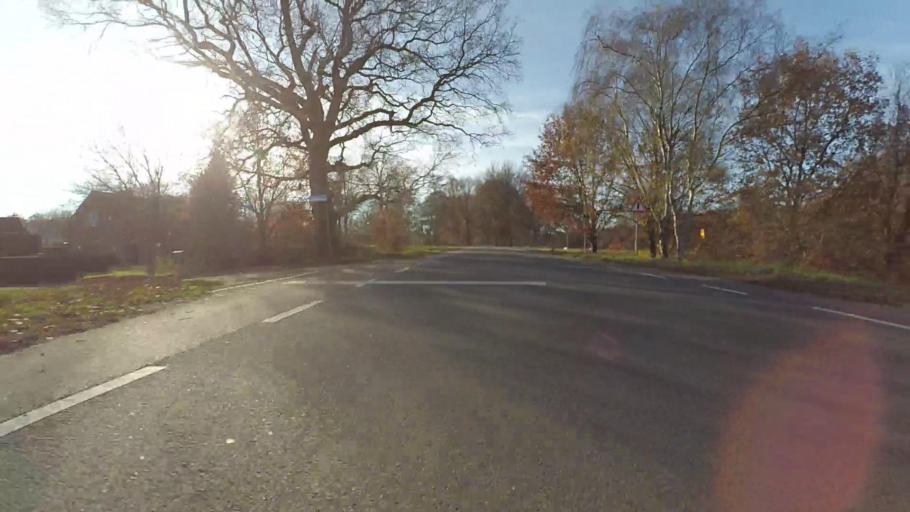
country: NL
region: Utrecht
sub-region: Gemeente Utrechtse Heuvelrug
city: Overberg
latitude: 52.0310
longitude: 5.5220
